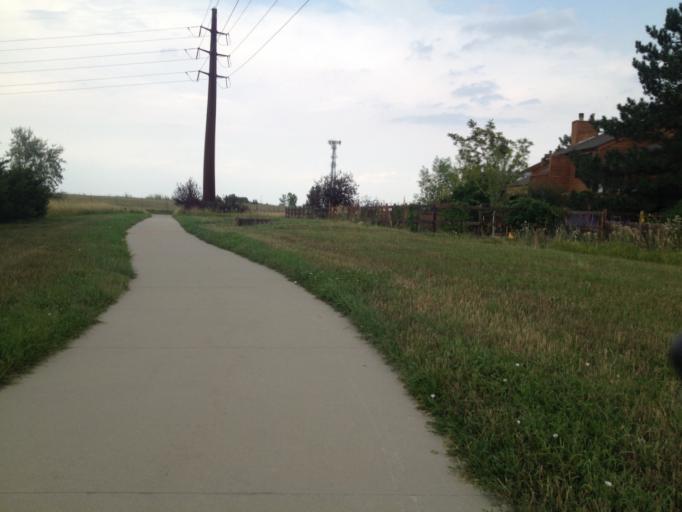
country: US
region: Colorado
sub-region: Boulder County
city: Louisville
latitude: 39.9890
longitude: -105.1563
